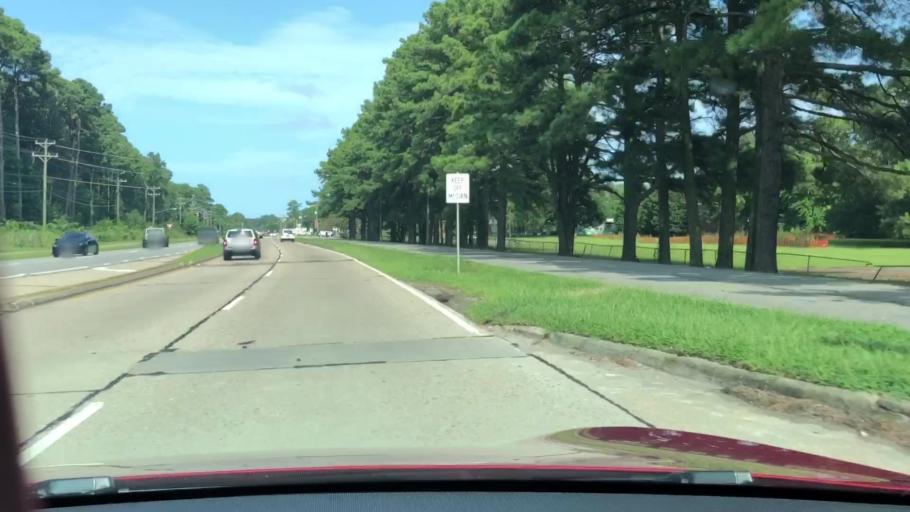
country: US
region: Virginia
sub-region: City of Virginia Beach
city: Virginia Beach
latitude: 36.8511
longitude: -76.0126
